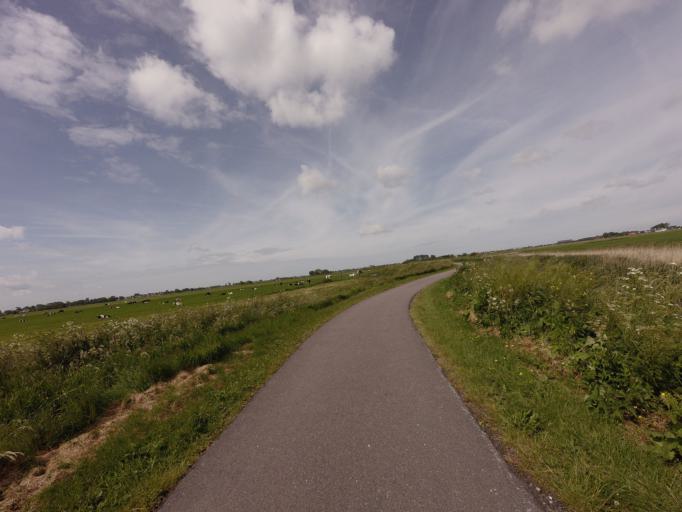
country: NL
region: North Holland
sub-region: Gemeente Opmeer
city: Opmeer
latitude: 52.6737
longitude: 4.9912
